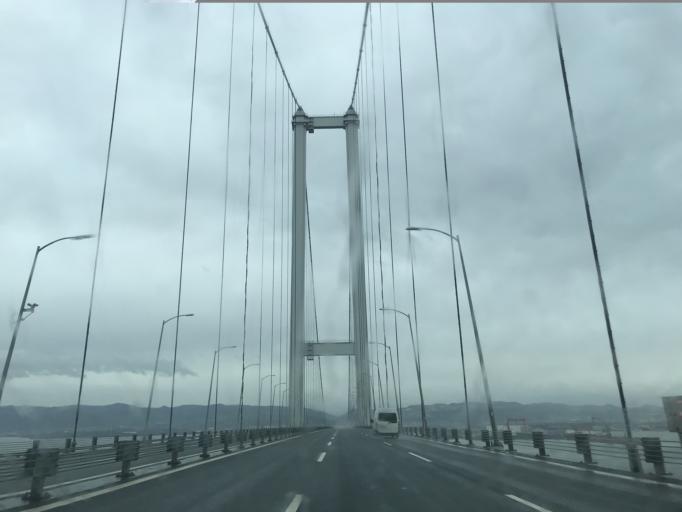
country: TR
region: Yalova
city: Altinova
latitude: 40.7509
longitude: 29.5151
